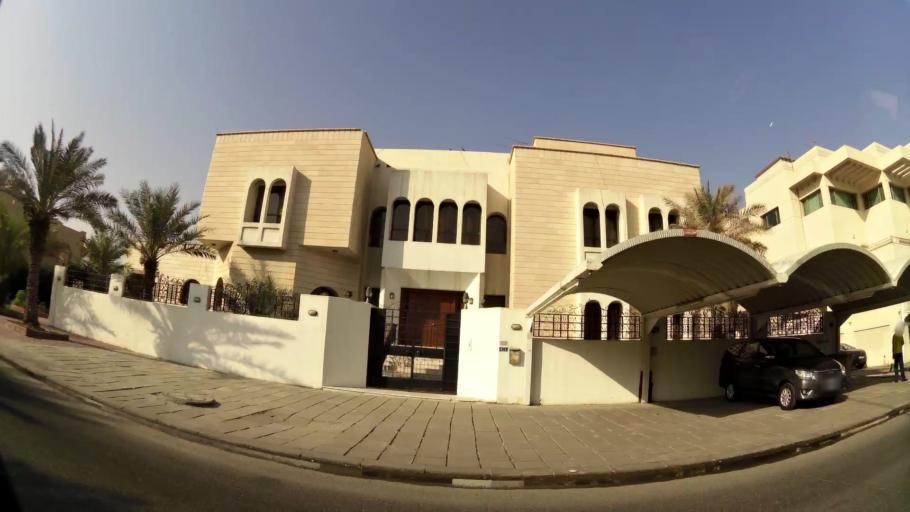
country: KW
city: Bayan
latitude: 29.3121
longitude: 48.0408
